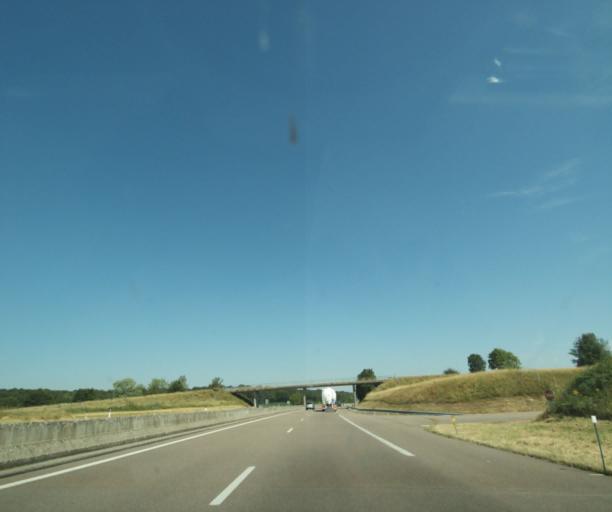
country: FR
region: Lorraine
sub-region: Departement des Vosges
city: Chatenois
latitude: 48.4108
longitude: 5.8675
